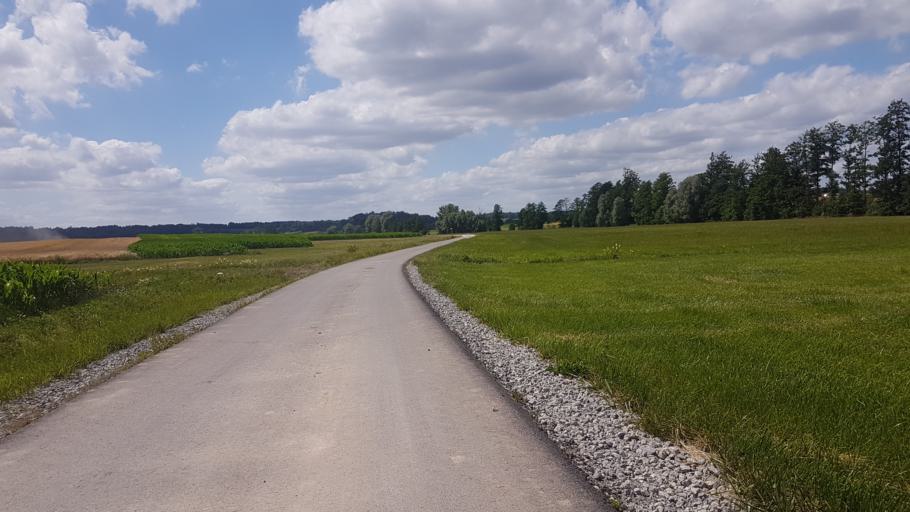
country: DE
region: Bavaria
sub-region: Regierungsbezirk Mittelfranken
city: Geslau
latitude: 49.3646
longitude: 10.3028
